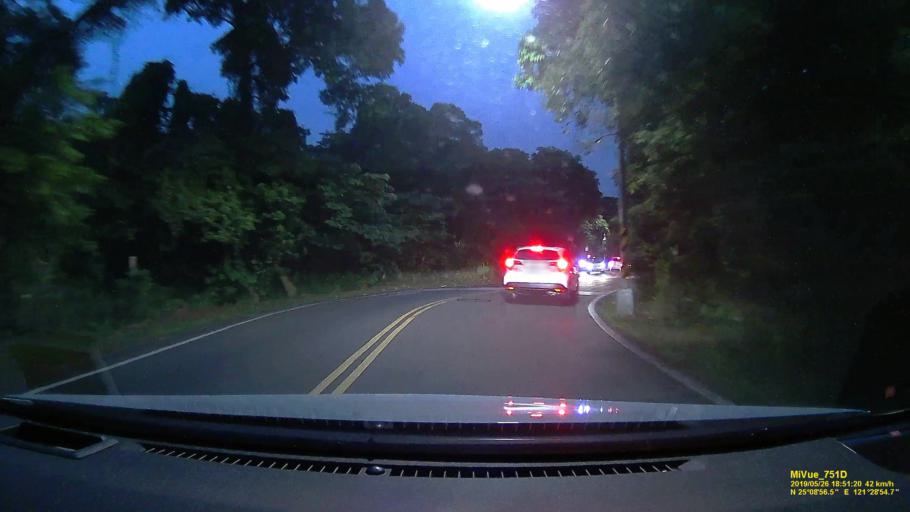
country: TW
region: Taipei
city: Taipei
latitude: 25.1488
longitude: 121.4818
